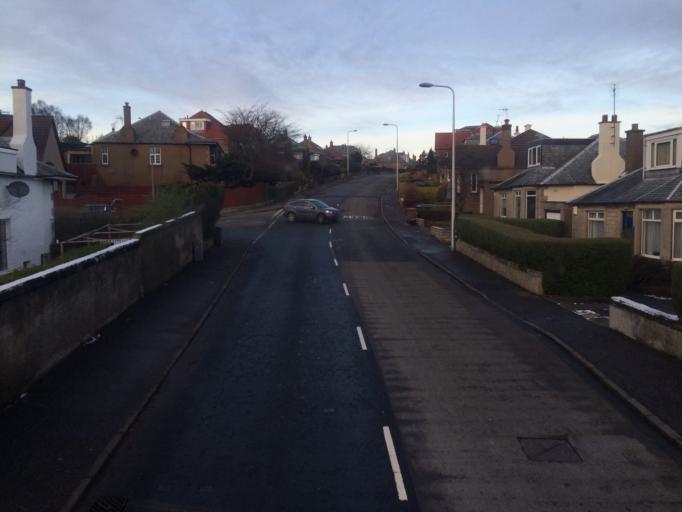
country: GB
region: Scotland
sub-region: Edinburgh
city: Colinton
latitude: 55.9120
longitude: -3.2186
